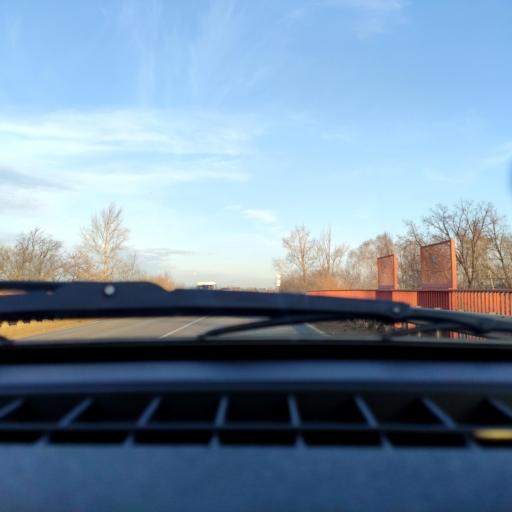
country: RU
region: Bashkortostan
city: Iglino
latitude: 54.7748
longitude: 56.2562
